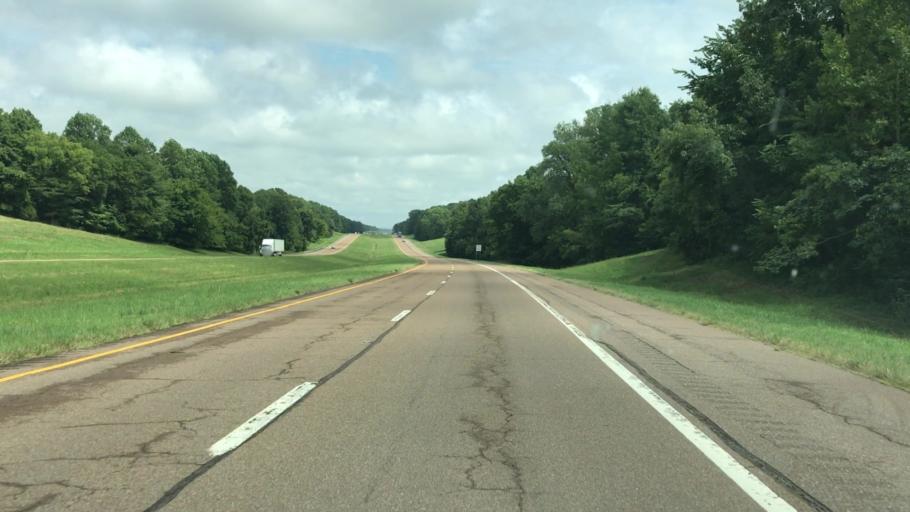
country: US
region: Tennessee
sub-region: Dyer County
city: Dyersburg
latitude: 36.0696
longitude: -89.4476
